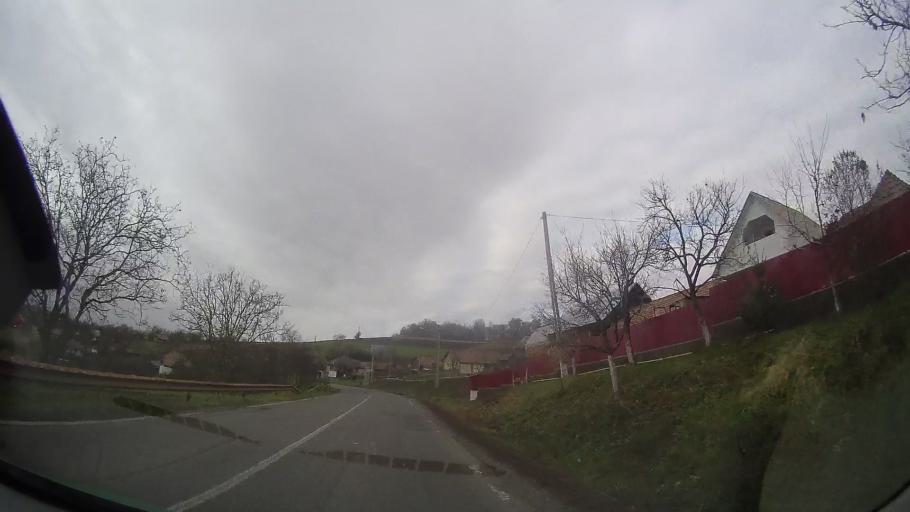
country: RO
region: Bistrita-Nasaud
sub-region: Comuna Silvasu de Campie
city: Silvasu de Campie
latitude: 46.7779
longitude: 24.3186
